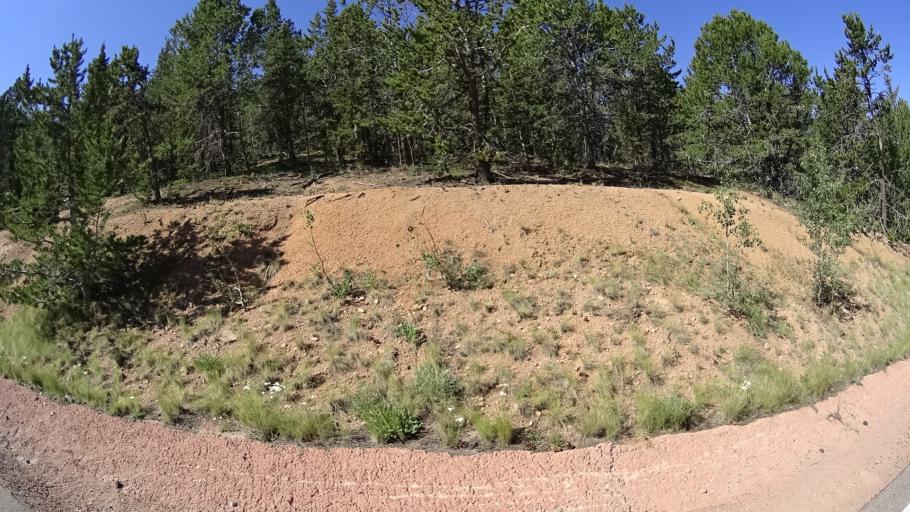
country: US
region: Colorado
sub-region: El Paso County
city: Cascade-Chipita Park
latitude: 38.8962
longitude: -105.0638
